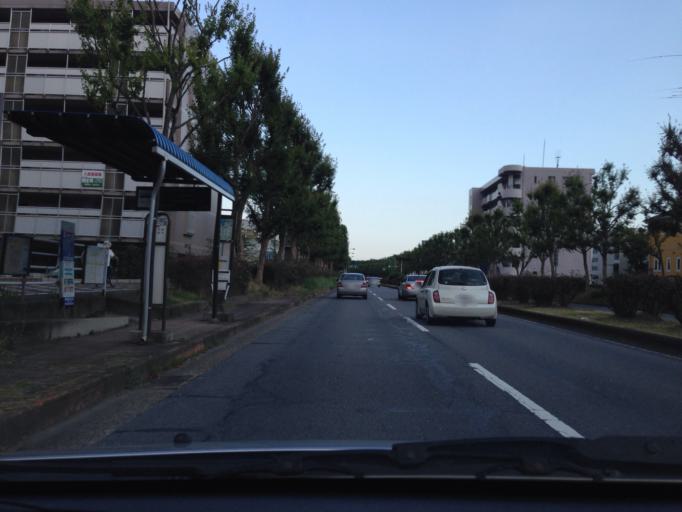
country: JP
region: Ibaraki
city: Naka
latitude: 36.0753
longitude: 140.1249
